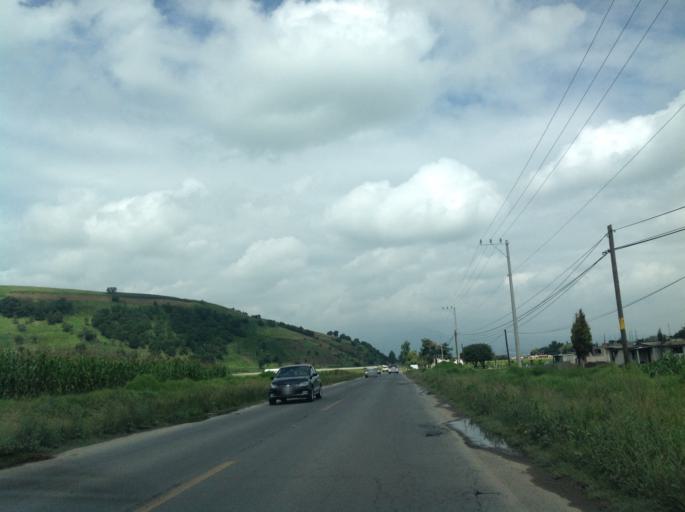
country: MX
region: Mexico
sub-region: Tenango del Valle
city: Santa Maria Jajalpa
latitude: 19.1164
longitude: -99.5433
